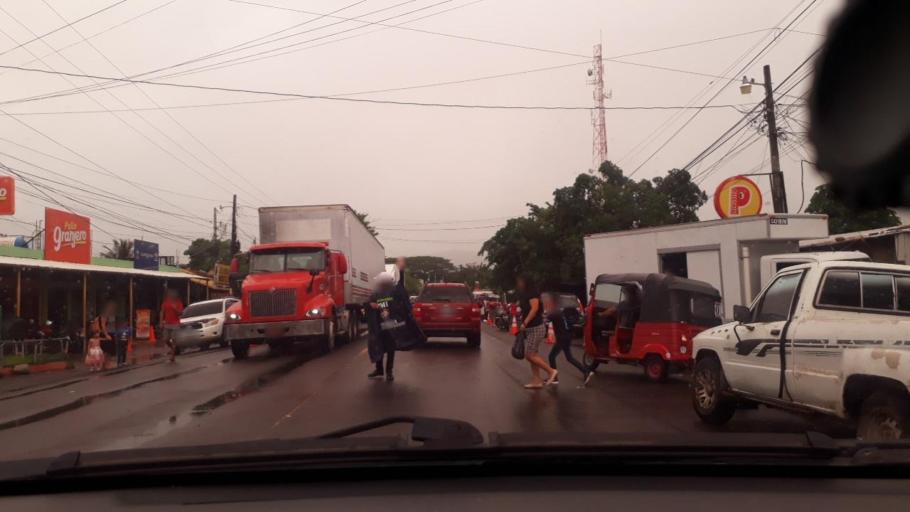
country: SV
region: Ahuachapan
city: San Francisco Menendez
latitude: 13.8739
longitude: -90.0962
